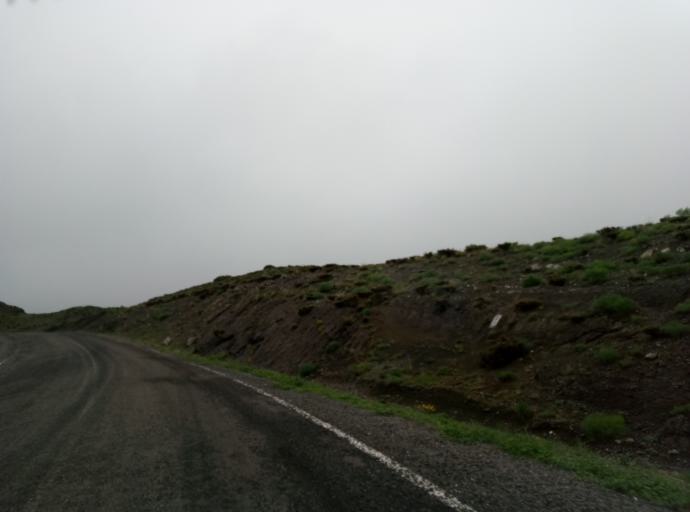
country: TR
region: Sivas
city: Serefiye
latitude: 40.1686
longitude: 37.8740
